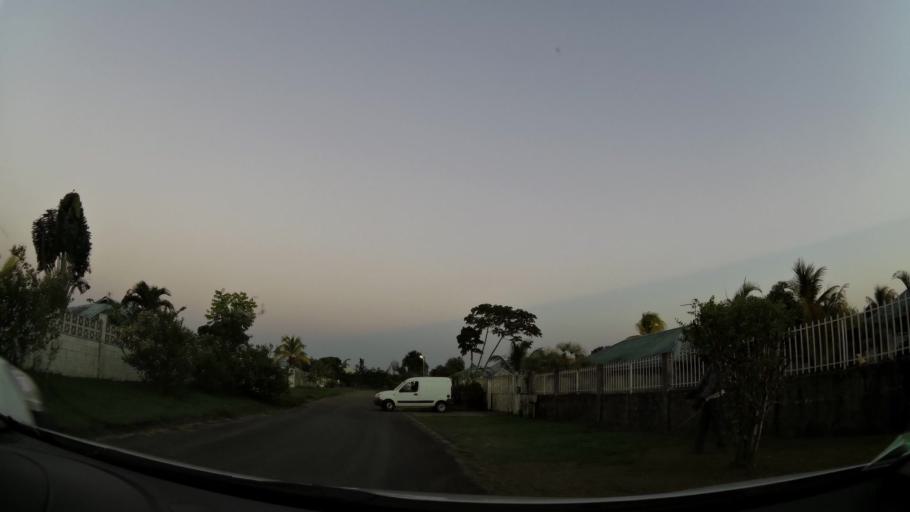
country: GF
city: Macouria
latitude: 4.9293
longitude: -52.4153
